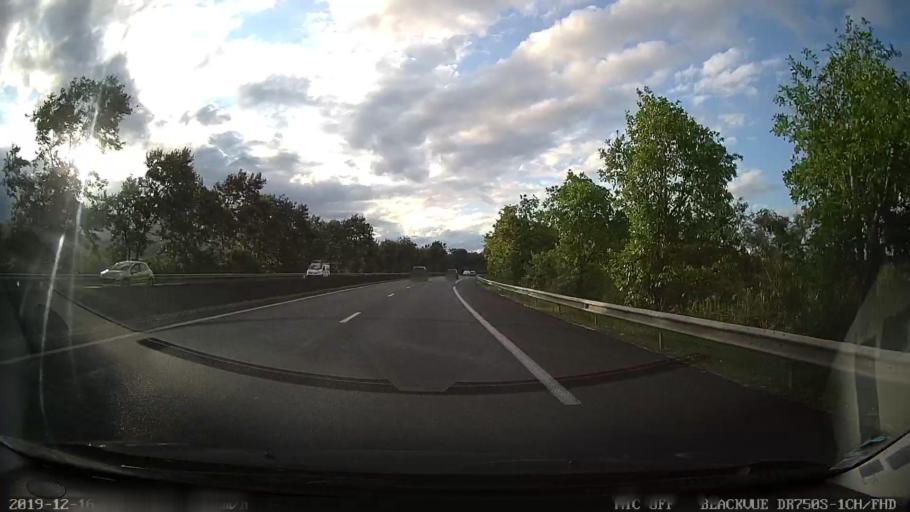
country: RE
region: Reunion
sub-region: Reunion
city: Bras-Panon
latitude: -21.0060
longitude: 55.6812
